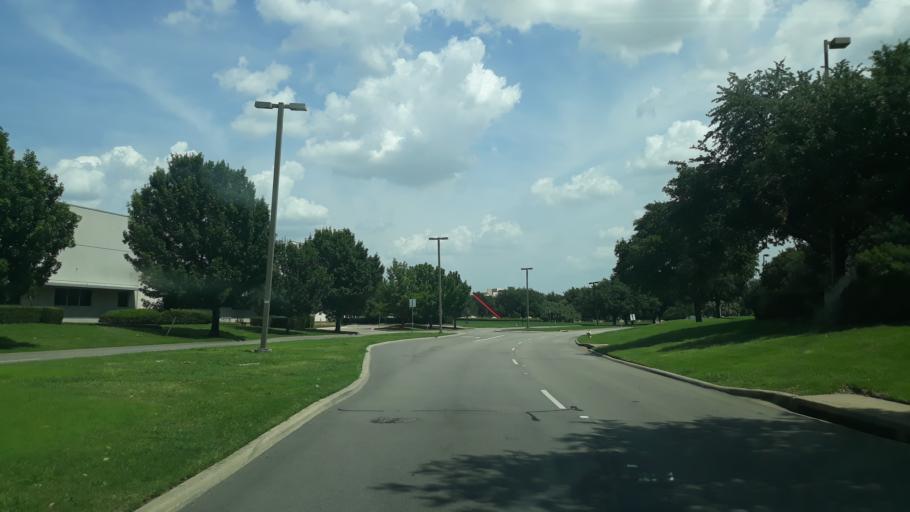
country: US
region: Texas
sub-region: Dallas County
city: Coppell
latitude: 32.9574
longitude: -97.0234
